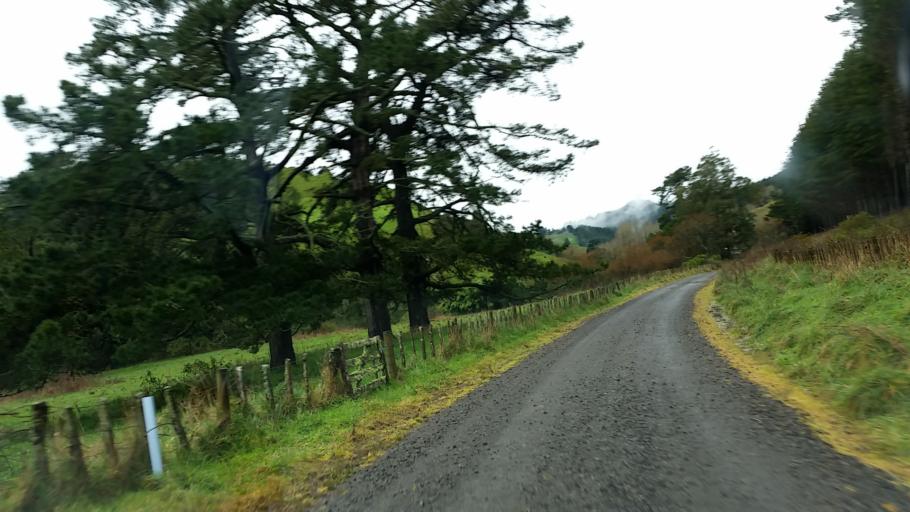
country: NZ
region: Taranaki
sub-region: South Taranaki District
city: Eltham
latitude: -39.5016
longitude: 174.4143
